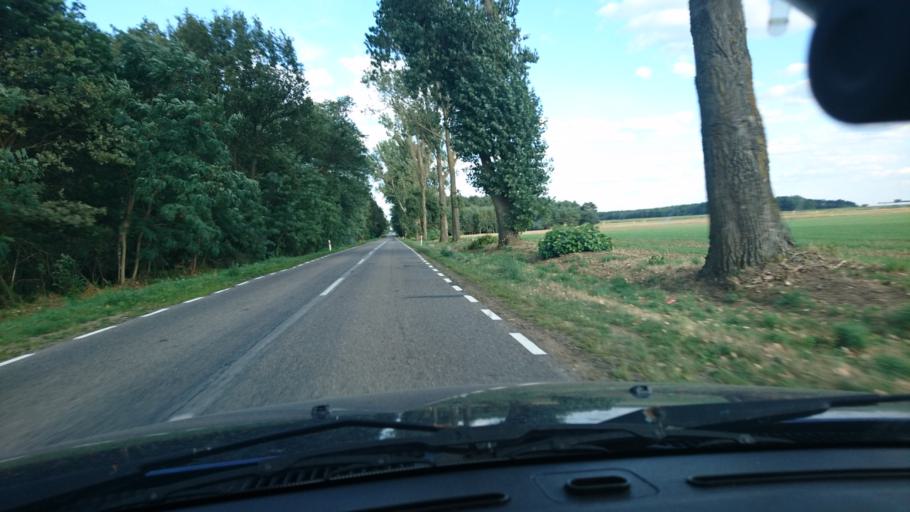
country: PL
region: Greater Poland Voivodeship
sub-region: Powiat ostrowski
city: Odolanow
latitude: 51.5932
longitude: 17.6262
